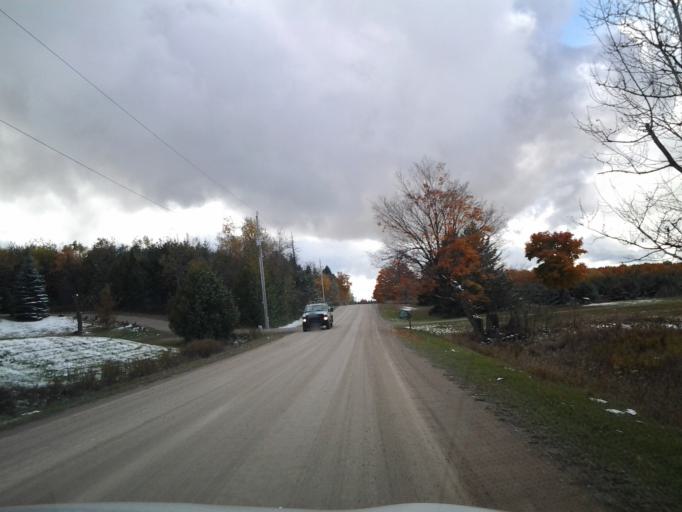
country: CA
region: Ontario
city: Shelburne
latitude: 44.0598
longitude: -80.1008
